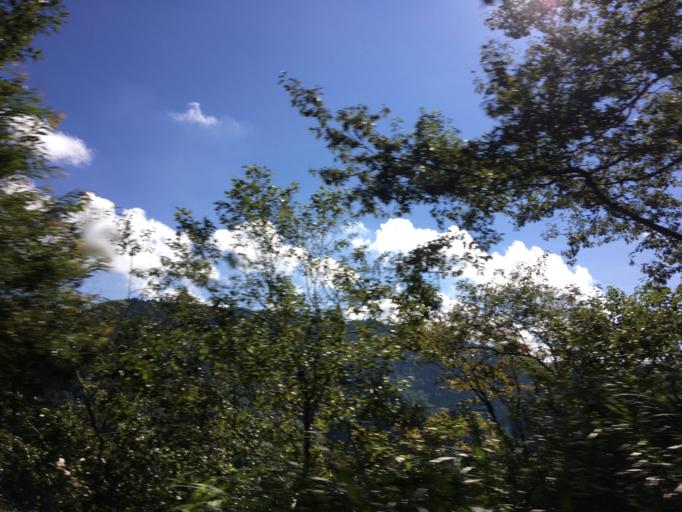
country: TW
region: Taiwan
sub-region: Yilan
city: Yilan
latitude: 24.5077
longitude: 121.5699
